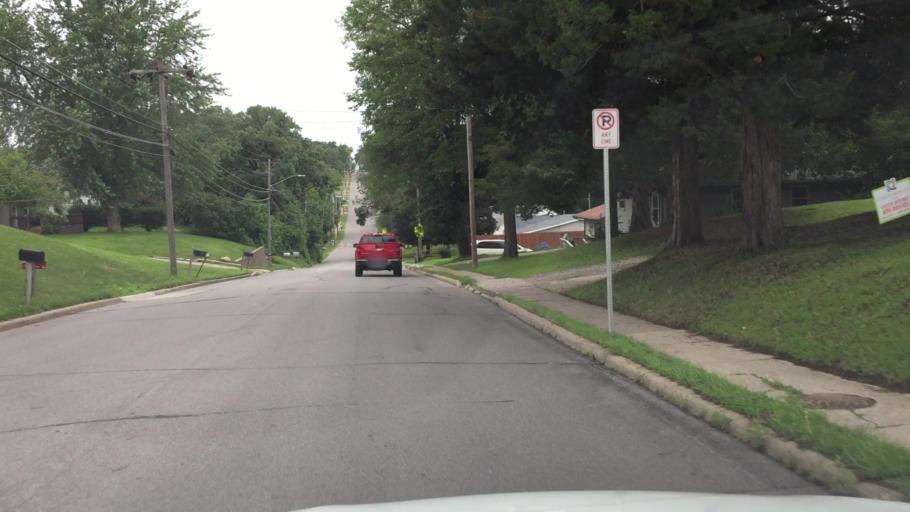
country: US
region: Iowa
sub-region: Jasper County
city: Newton
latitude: 41.7082
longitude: -93.0532
